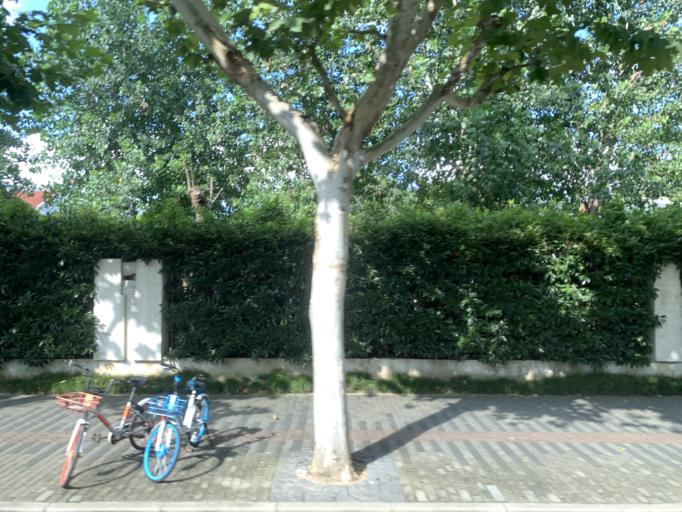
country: CN
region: Shanghai Shi
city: Pudong
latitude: 31.2471
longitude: 121.5615
